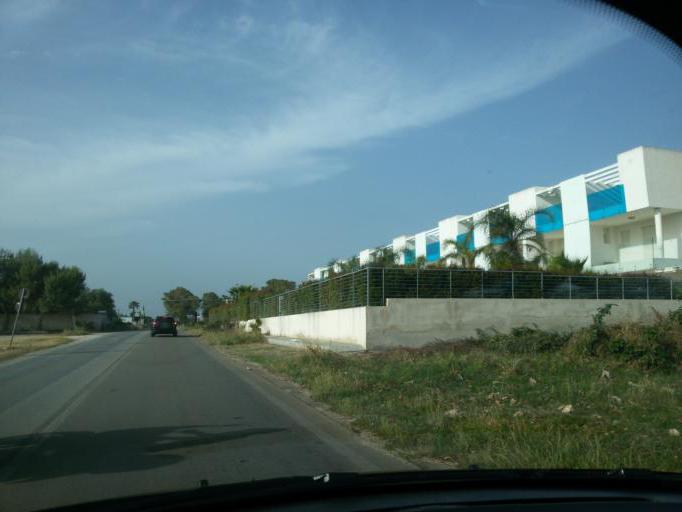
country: IT
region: Apulia
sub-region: Provincia di Lecce
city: Porto Cesareo
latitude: 40.2971
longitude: 17.8564
